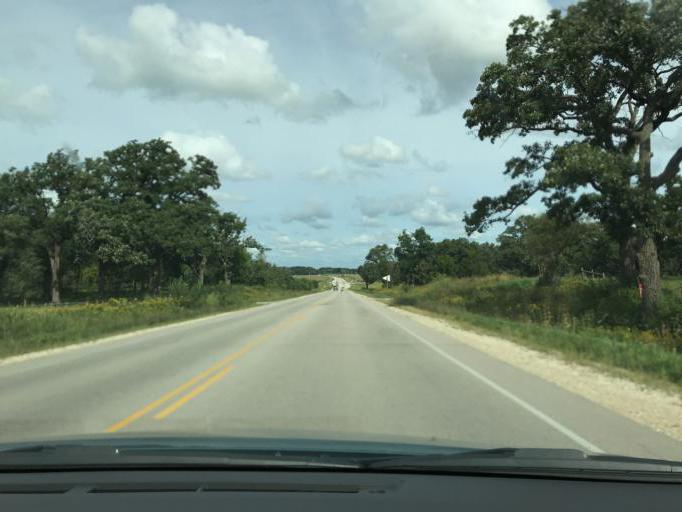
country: US
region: Wisconsin
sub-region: Racine County
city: Bohners Lake
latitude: 42.6060
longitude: -88.2259
